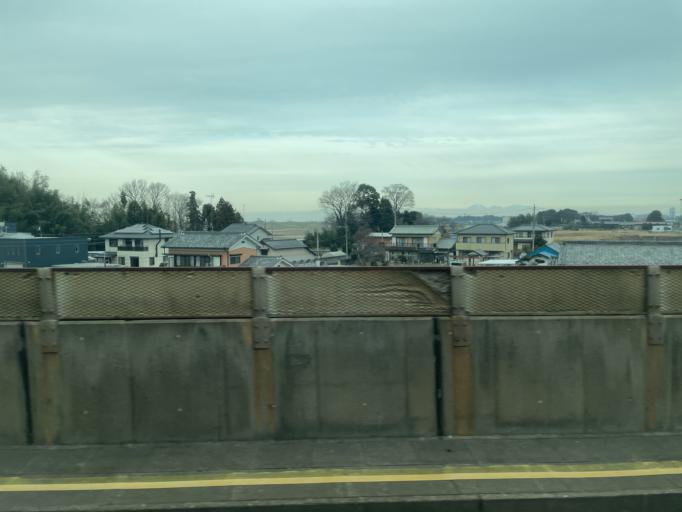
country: JP
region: Saitama
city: Kurihashi
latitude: 36.1510
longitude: 139.7068
